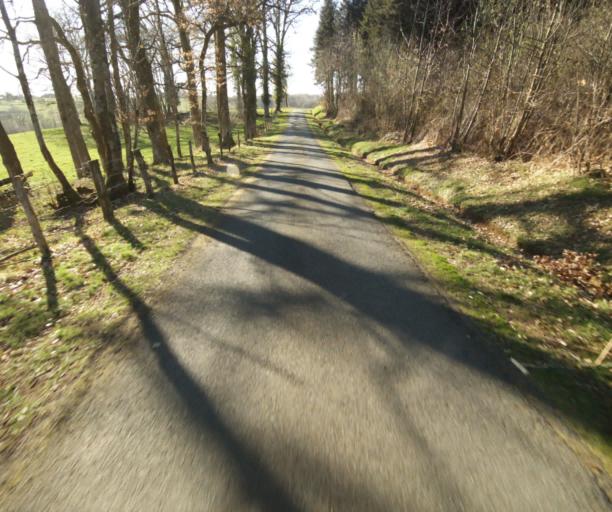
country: FR
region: Limousin
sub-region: Departement de la Correze
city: Seilhac
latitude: 45.3847
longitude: 1.6977
